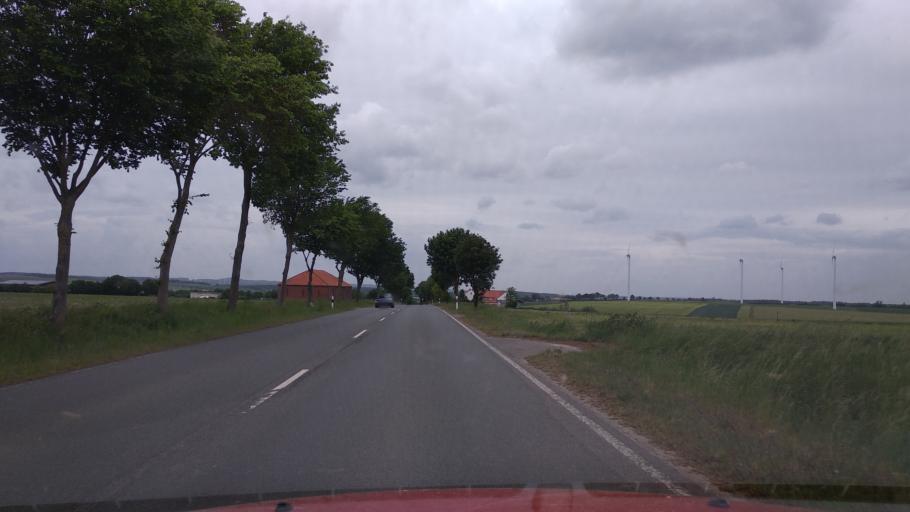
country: DE
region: North Rhine-Westphalia
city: Borgentreich
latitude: 51.5850
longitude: 9.1535
